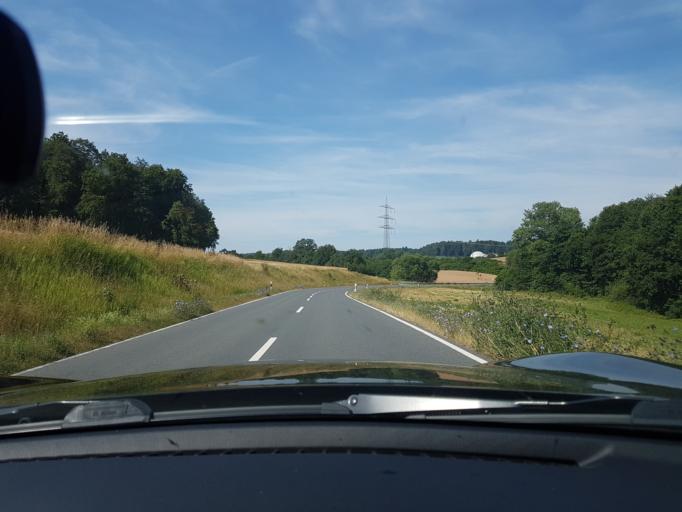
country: DE
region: Baden-Wuerttemberg
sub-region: Karlsruhe Region
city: Seckach
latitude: 49.4439
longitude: 9.3220
